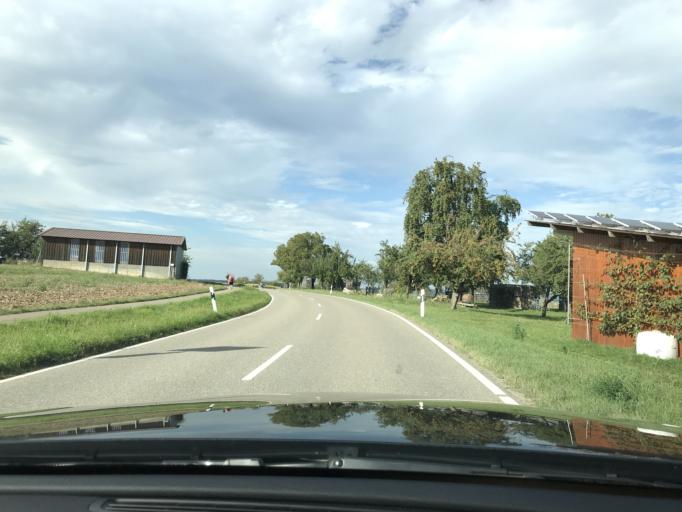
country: DE
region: Baden-Wuerttemberg
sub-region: Regierungsbezirk Stuttgart
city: Affalterbach
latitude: 48.9260
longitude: 9.3250
